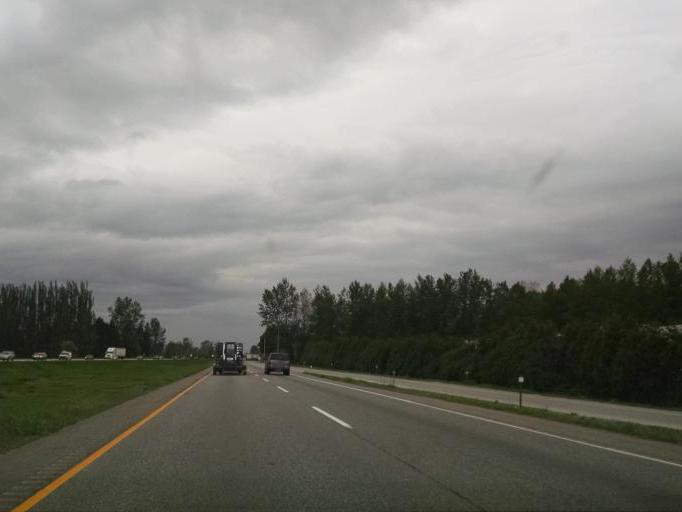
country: CA
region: British Columbia
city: Abbotsford
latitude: 49.0624
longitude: -122.1694
